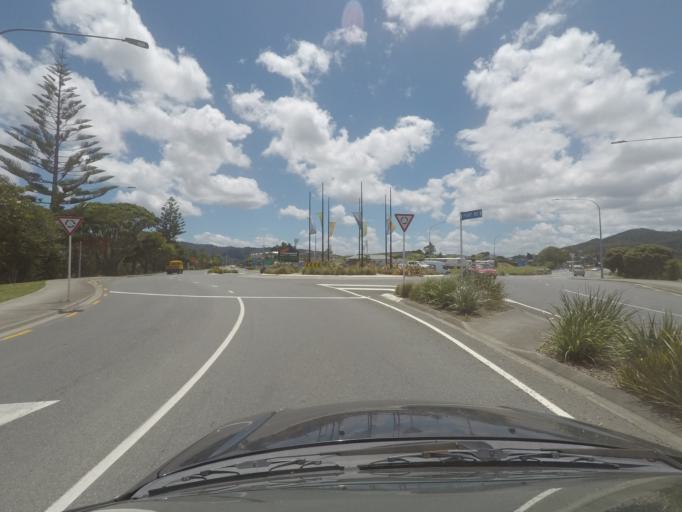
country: NZ
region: Northland
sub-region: Whangarei
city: Whangarei
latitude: -35.7372
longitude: 174.3327
